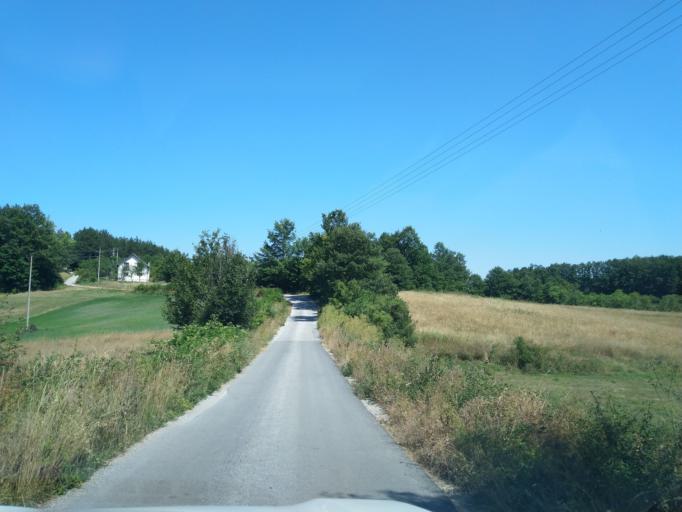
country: RS
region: Central Serbia
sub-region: Zlatiborski Okrug
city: Uzice
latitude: 43.8048
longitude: 19.8382
